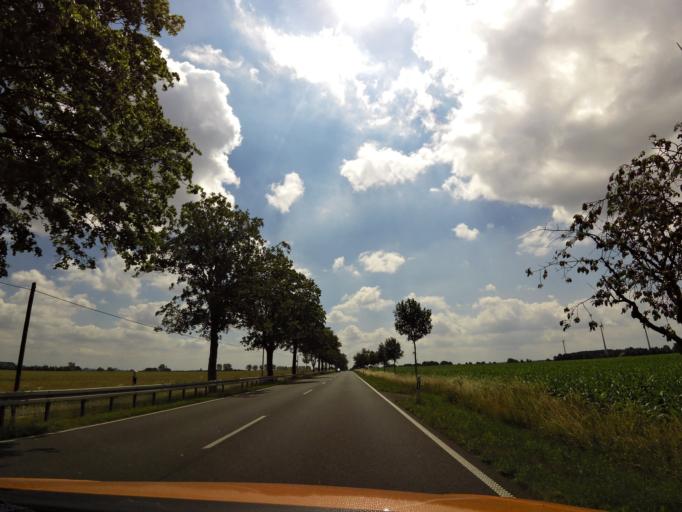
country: DE
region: Brandenburg
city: Wusterhausen
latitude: 52.8586
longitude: 12.4958
